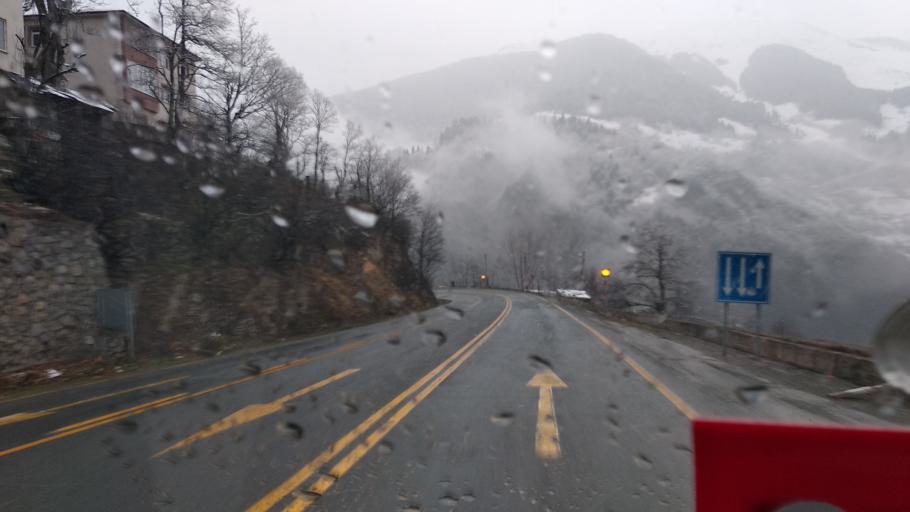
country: TR
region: Gumushane
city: Yaglidere
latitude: 40.6991
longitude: 39.4824
